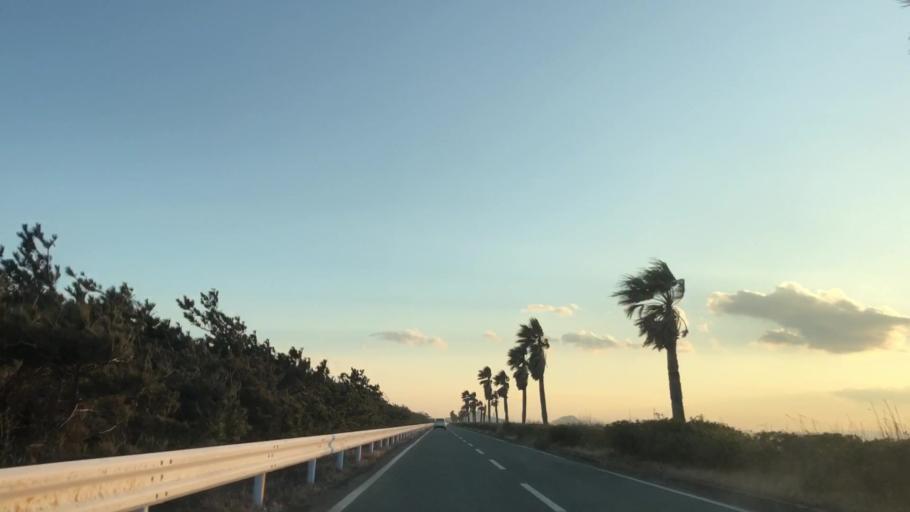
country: JP
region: Aichi
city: Toyohama
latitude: 34.6282
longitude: 137.0469
